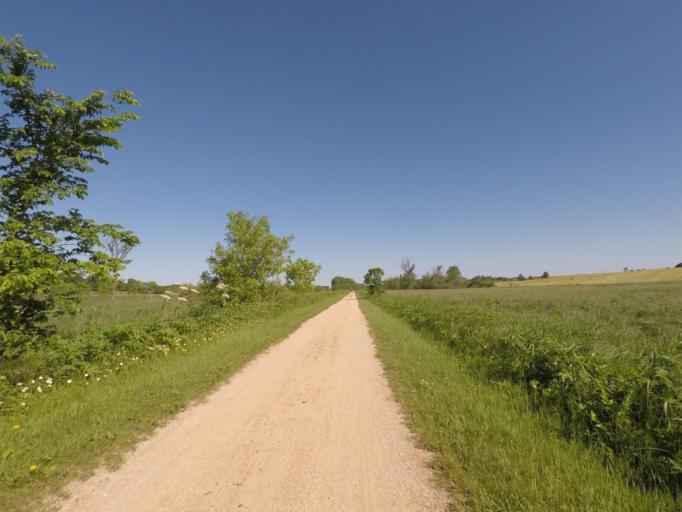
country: US
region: Wisconsin
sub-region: Dane County
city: Verona
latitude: 43.0011
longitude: -89.5868
